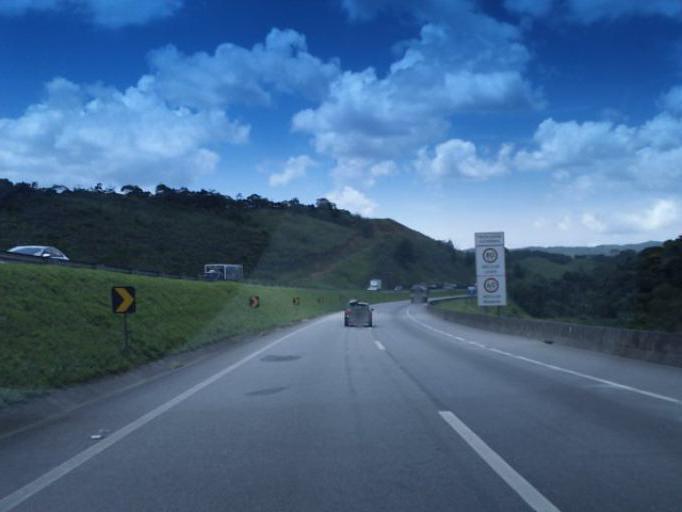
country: BR
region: Sao Paulo
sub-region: Juquitiba
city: Juquitiba
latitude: -23.9937
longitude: -47.1476
